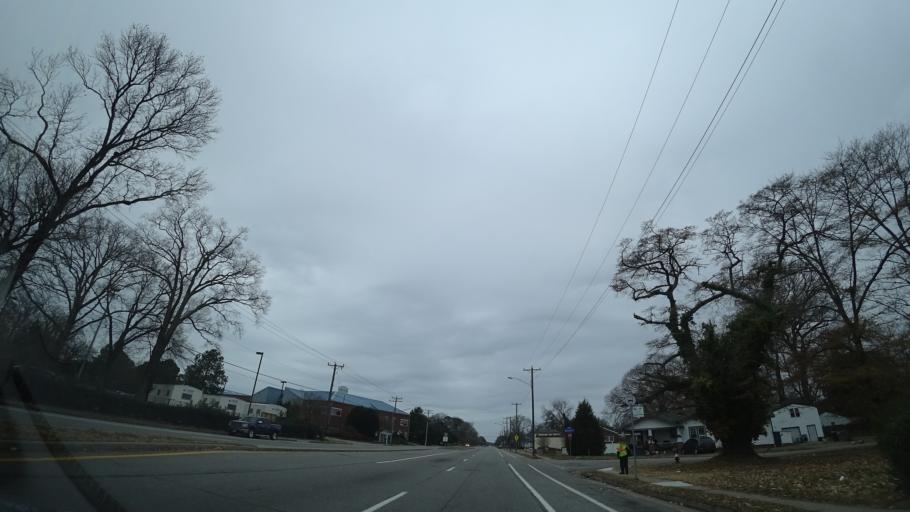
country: US
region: Virginia
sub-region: City of Hampton
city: Hampton
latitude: 37.0151
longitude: -76.3637
